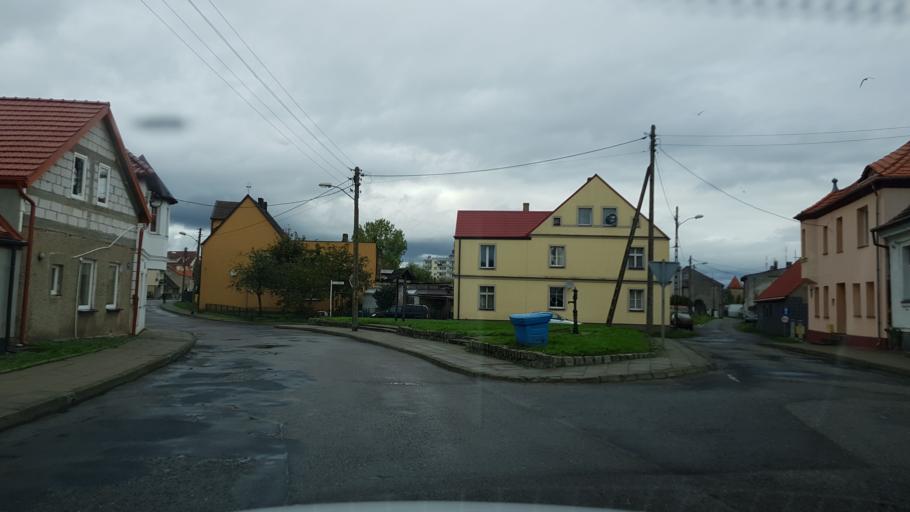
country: PL
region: West Pomeranian Voivodeship
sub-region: Powiat kamienski
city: Wolin
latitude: 53.8389
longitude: 14.6152
